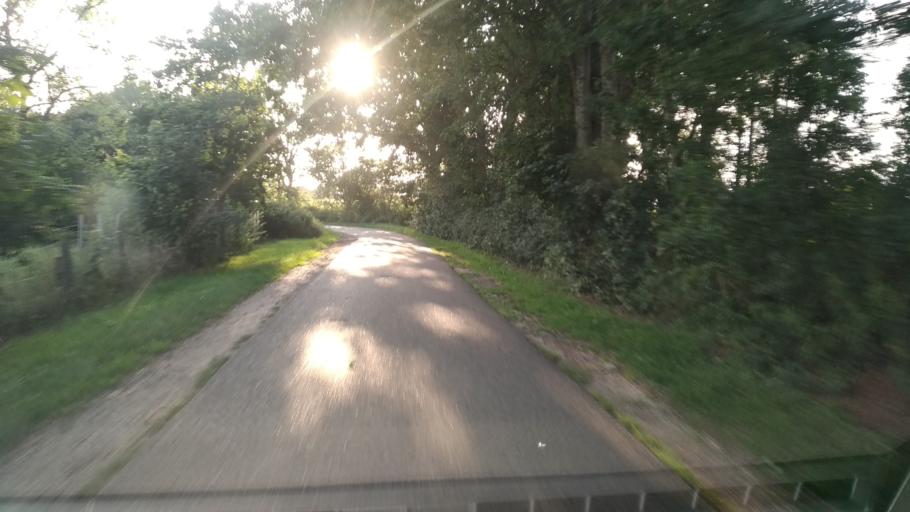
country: DE
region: Schleswig-Holstein
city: Klein Bennebek
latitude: 54.4198
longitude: 9.4554
